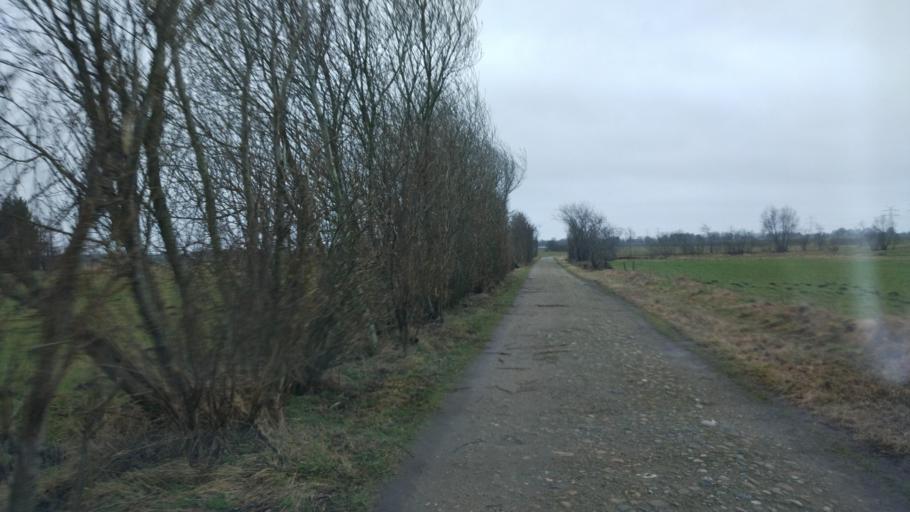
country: DE
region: Schleswig-Holstein
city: Gross Rheide
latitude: 54.4566
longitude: 9.4339
